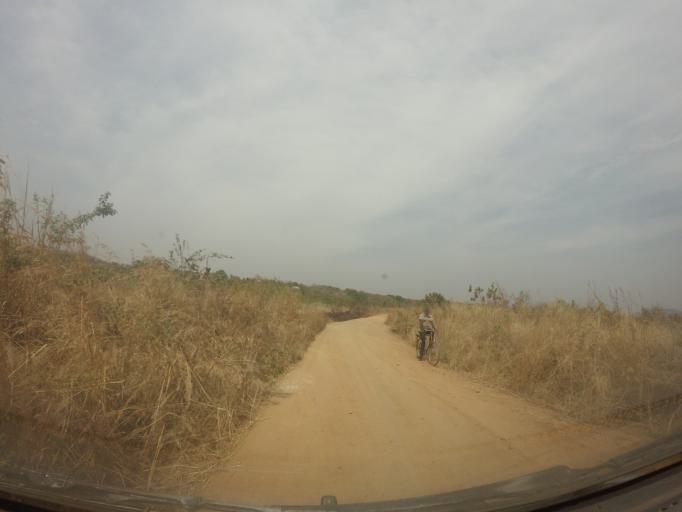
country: UG
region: Northern Region
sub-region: Zombo District
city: Zombo
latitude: 2.6830
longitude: 31.0234
